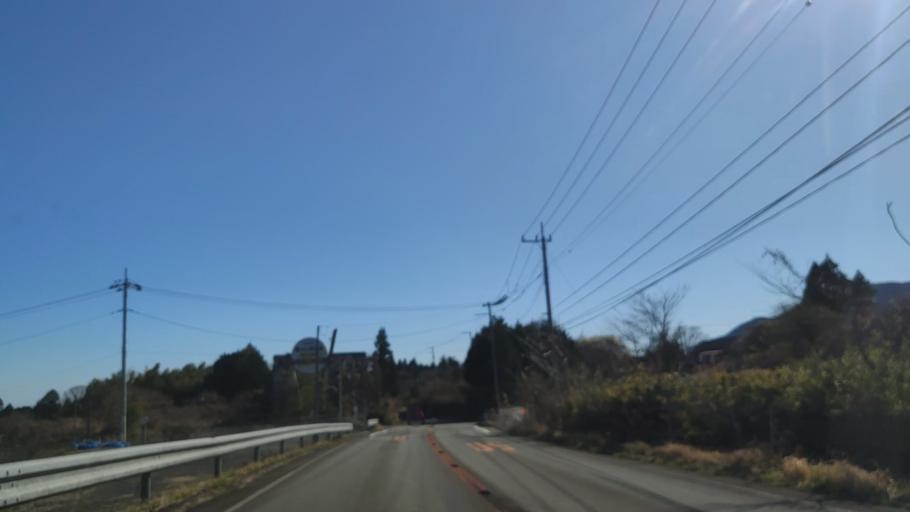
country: JP
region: Shizuoka
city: Fujinomiya
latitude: 35.3198
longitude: 138.5855
